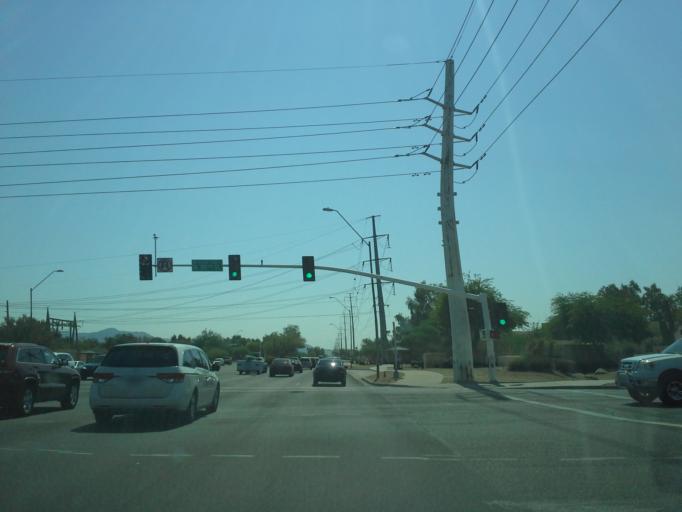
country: US
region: Arizona
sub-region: Maricopa County
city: Scottsdale
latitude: 33.5825
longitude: -111.8863
